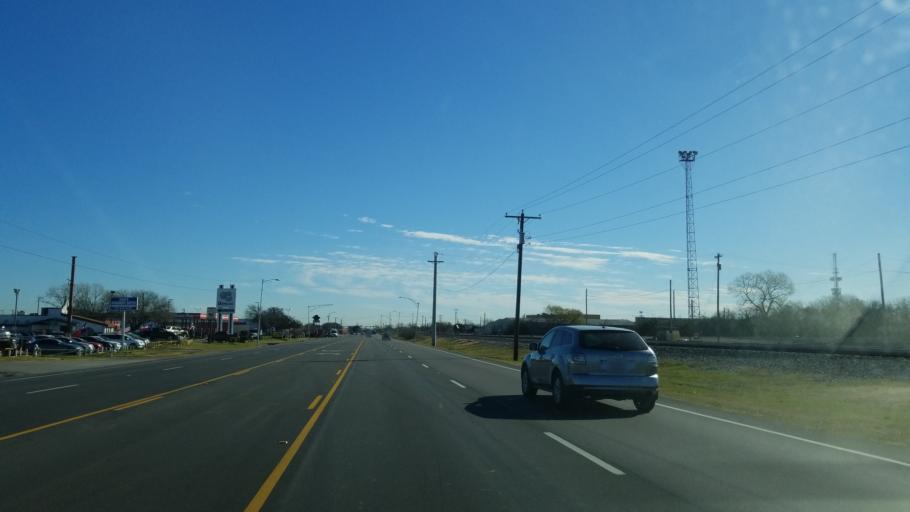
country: US
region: Texas
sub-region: Dallas County
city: Grand Prairie
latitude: 32.7405
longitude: -97.0513
